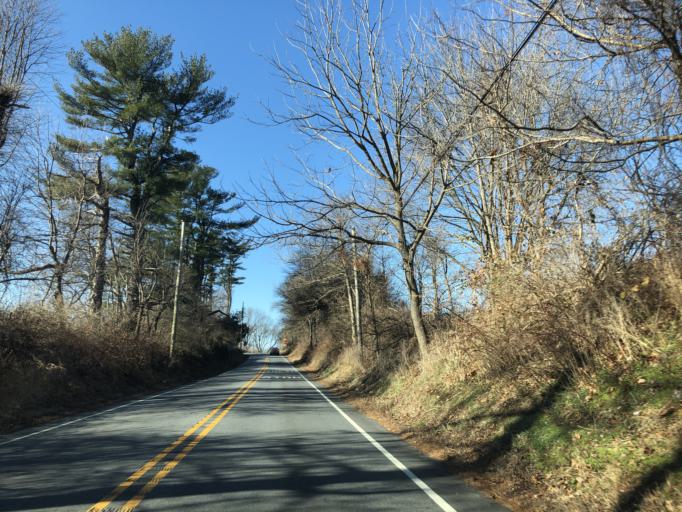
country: US
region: Pennsylvania
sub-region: Chester County
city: Upland
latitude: 39.9021
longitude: -75.7808
